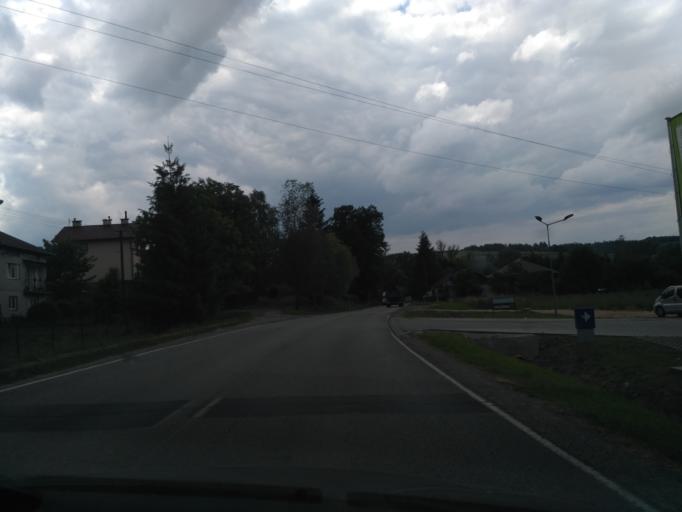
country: PL
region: Subcarpathian Voivodeship
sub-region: Powiat rzeszowski
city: Chmielnik
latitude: 49.9413
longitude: 22.1032
